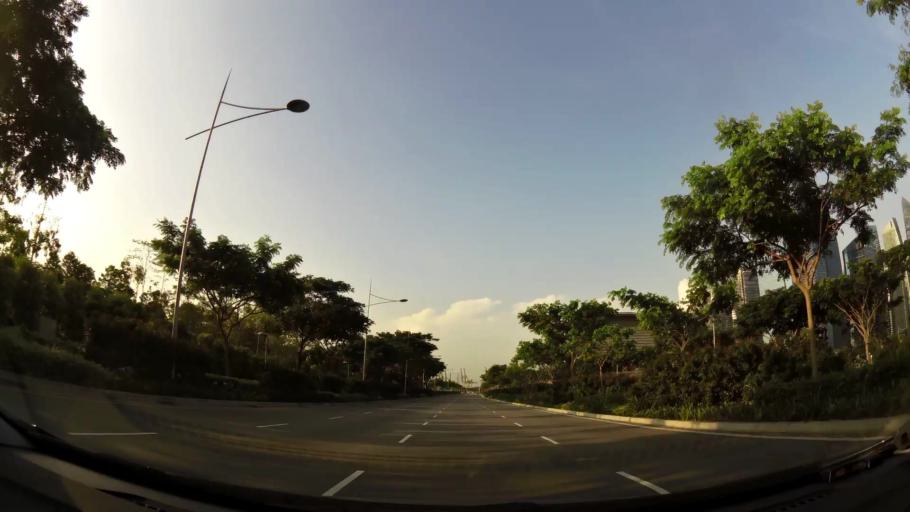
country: SG
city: Singapore
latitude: 1.2807
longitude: 103.8602
